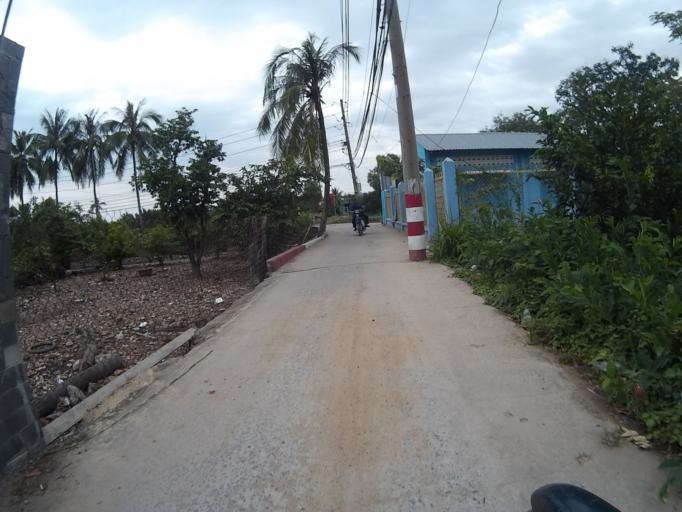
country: VN
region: Ho Chi Minh City
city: Quan Hai
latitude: 10.8187
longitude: 106.7430
